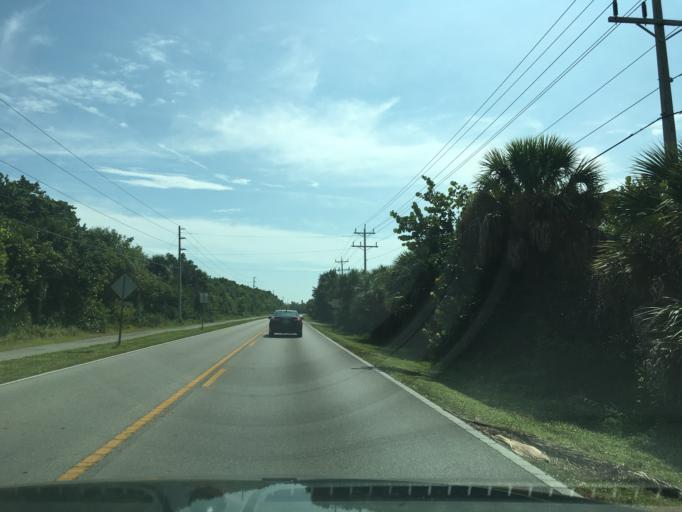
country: US
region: Florida
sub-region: Lee County
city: Saint James City
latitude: 26.4609
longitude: -82.1469
